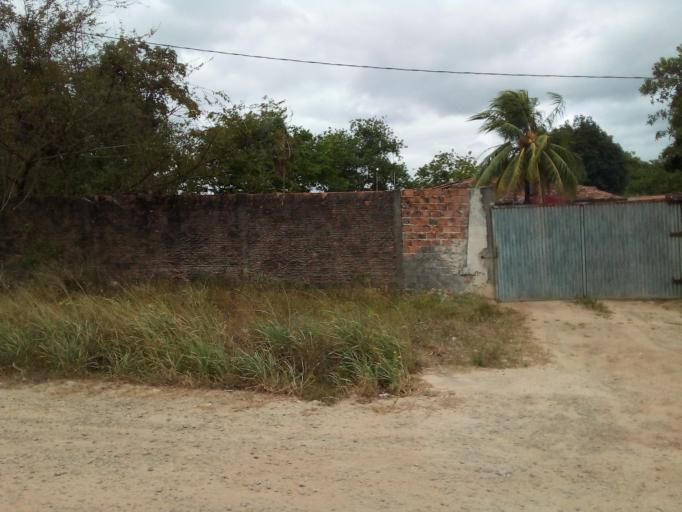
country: BR
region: Maranhao
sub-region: Sao Luis
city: Sao Luis
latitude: -2.6719
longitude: -44.2950
